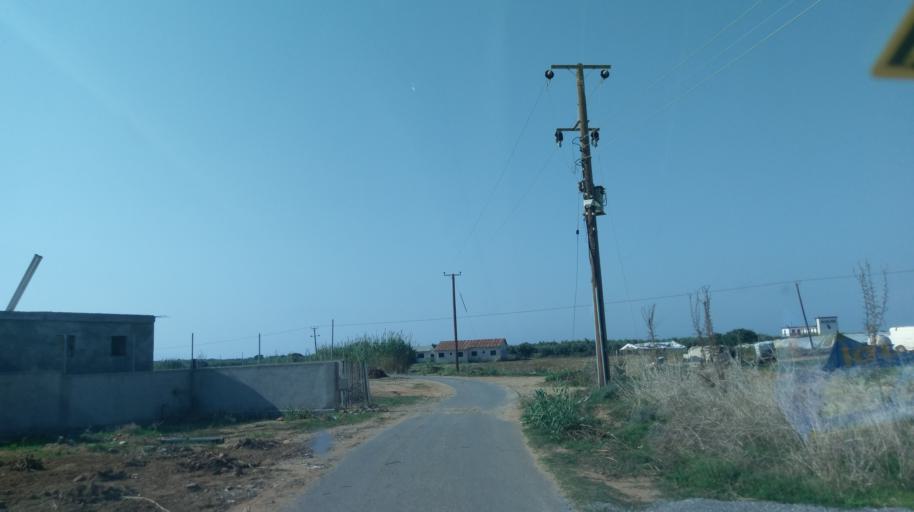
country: CY
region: Lefkosia
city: Morfou
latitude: 35.2959
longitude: 32.9568
